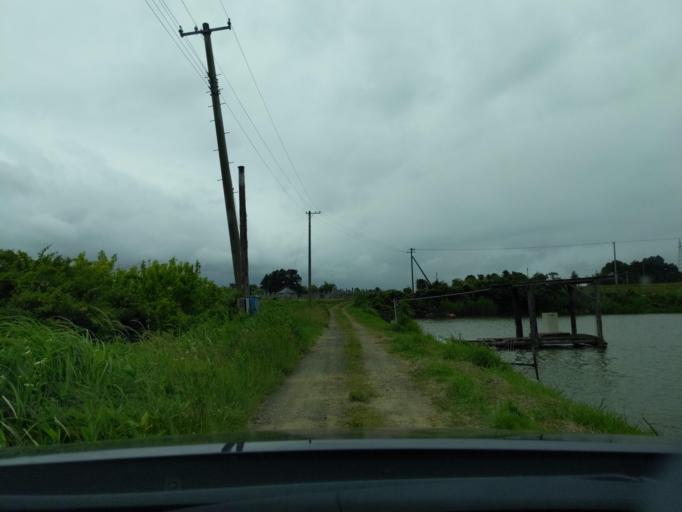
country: JP
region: Fukushima
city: Koriyama
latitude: 37.3683
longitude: 140.3173
